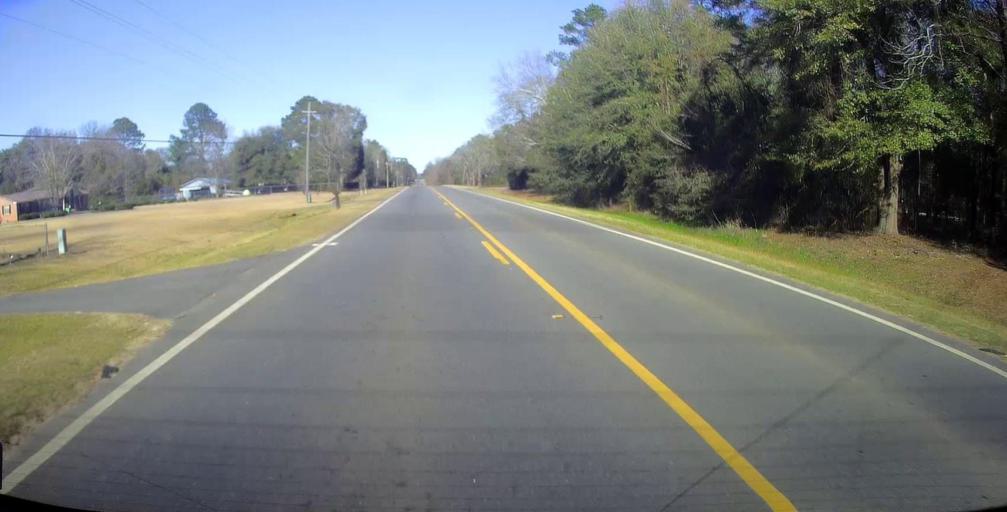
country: US
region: Georgia
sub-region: Macon County
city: Oglethorpe
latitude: 32.2741
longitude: -84.0785
